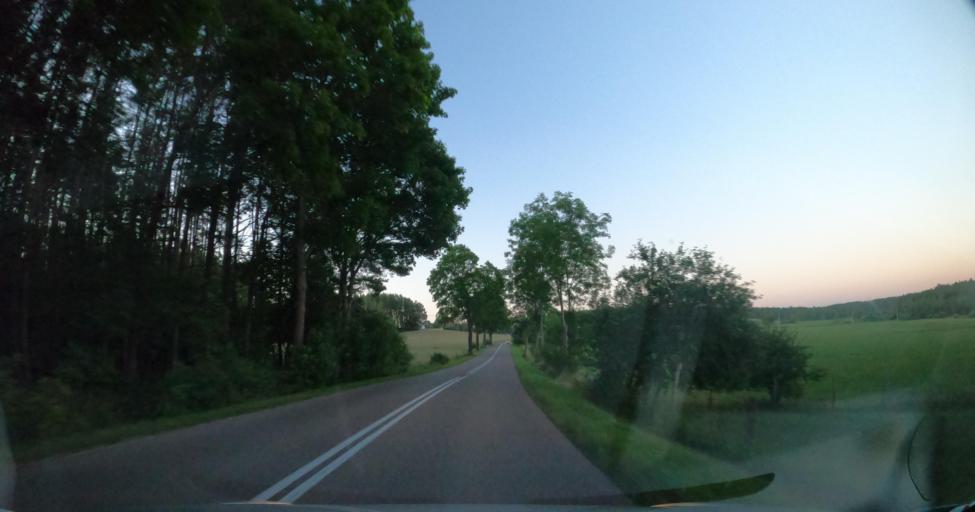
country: PL
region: Pomeranian Voivodeship
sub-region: Powiat wejherowski
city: Luzino
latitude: 54.4654
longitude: 18.0630
